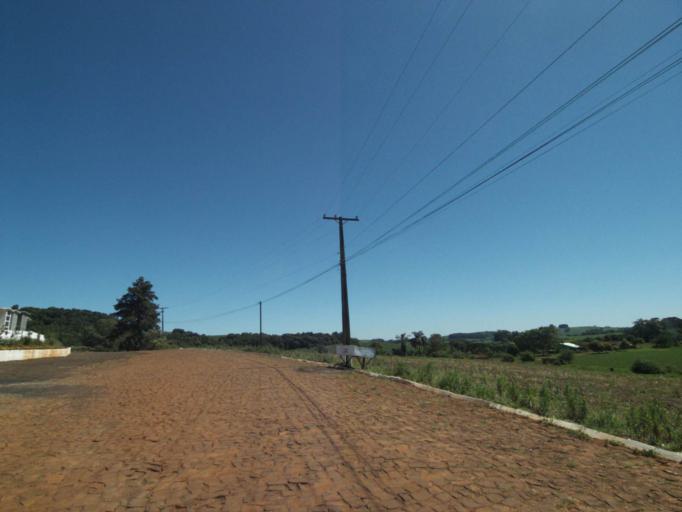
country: BR
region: Parana
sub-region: Pato Branco
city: Pato Branco
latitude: -26.2569
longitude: -52.7825
